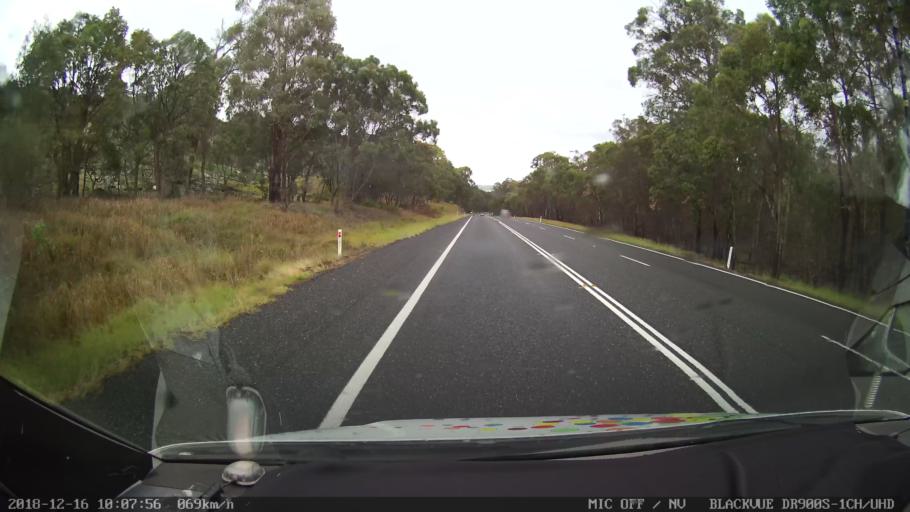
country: AU
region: New South Wales
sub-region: Glen Innes Severn
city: Glen Innes
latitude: -29.3328
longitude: 151.9005
